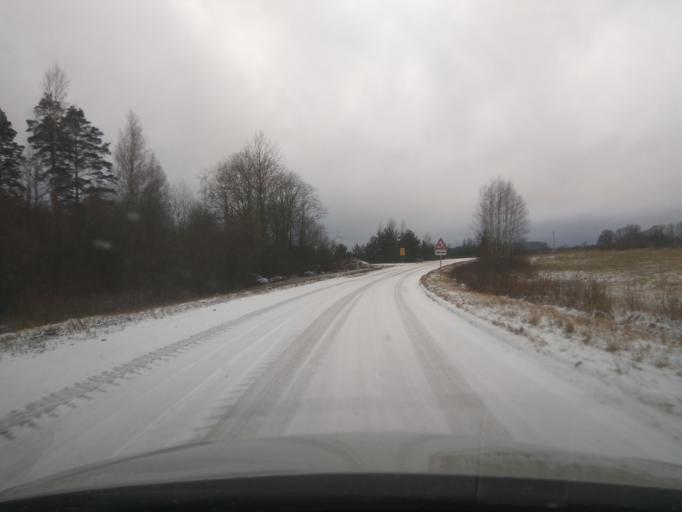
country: LV
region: Saldus Rajons
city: Saldus
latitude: 56.8103
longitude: 22.3251
